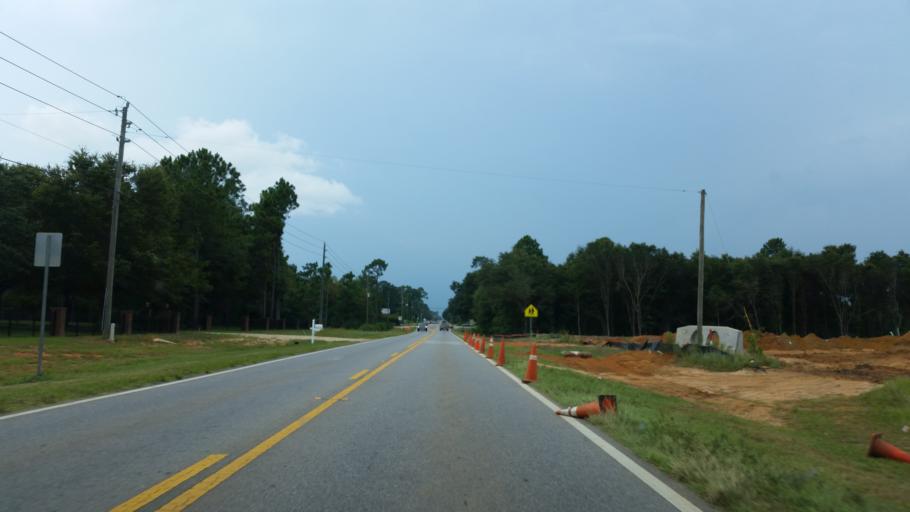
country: US
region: Florida
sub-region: Santa Rosa County
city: Pace
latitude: 30.6316
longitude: -87.1701
